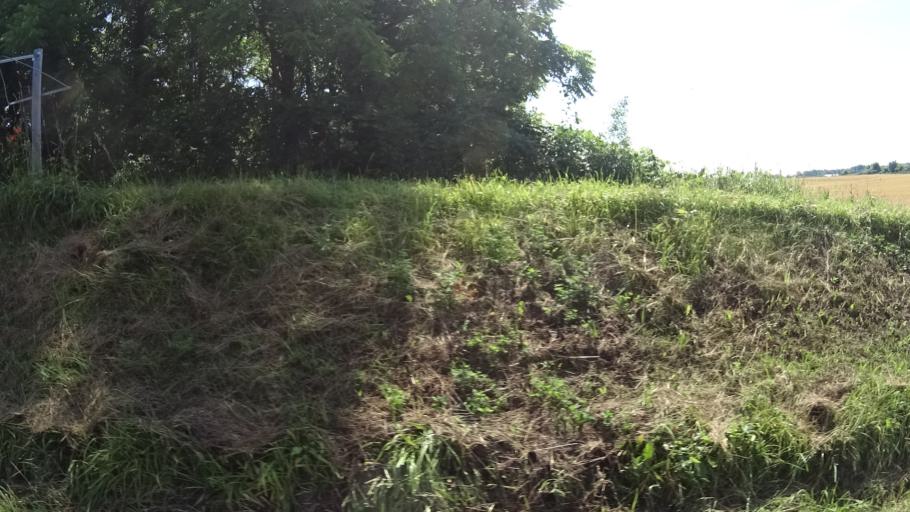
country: US
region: Ohio
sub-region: Erie County
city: Huron
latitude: 41.3785
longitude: -82.4722
